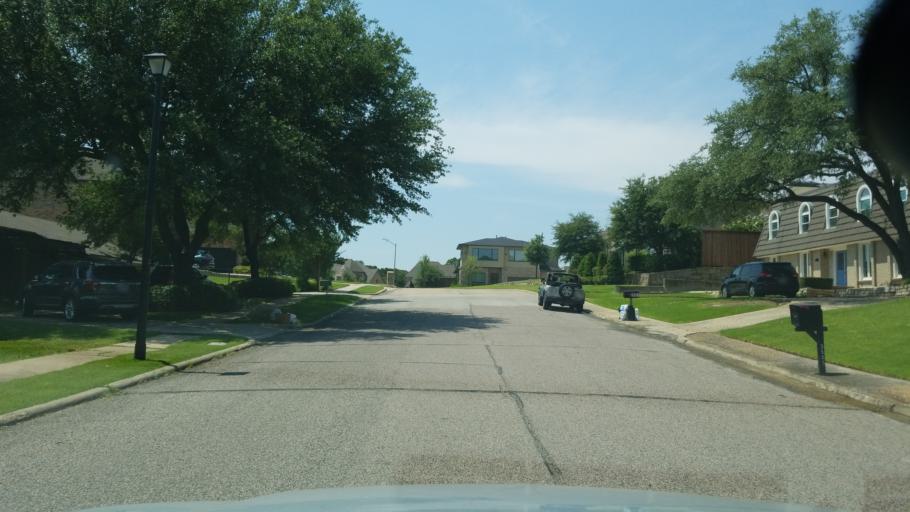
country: US
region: Texas
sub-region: Dallas County
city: Irving
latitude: 32.8500
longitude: -96.9424
